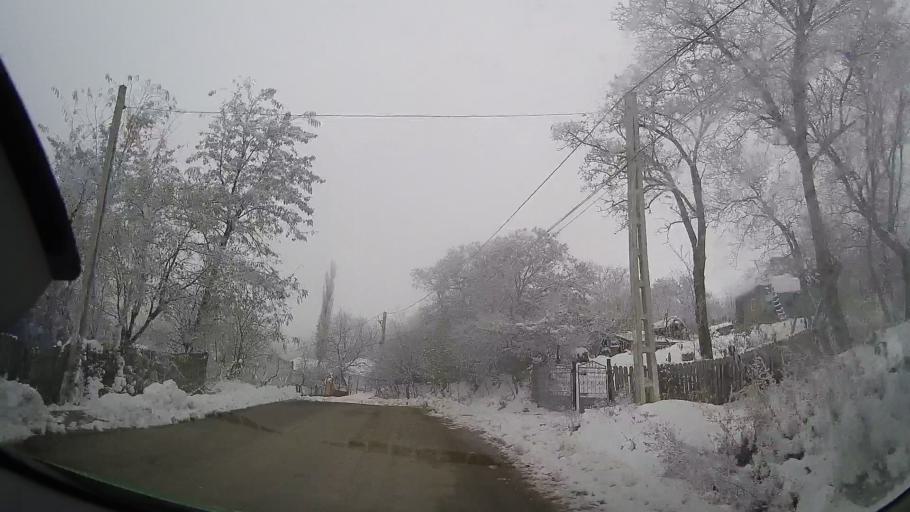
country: RO
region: Iasi
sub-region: Comuna Tansa
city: Suhulet
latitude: 46.8943
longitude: 27.2827
